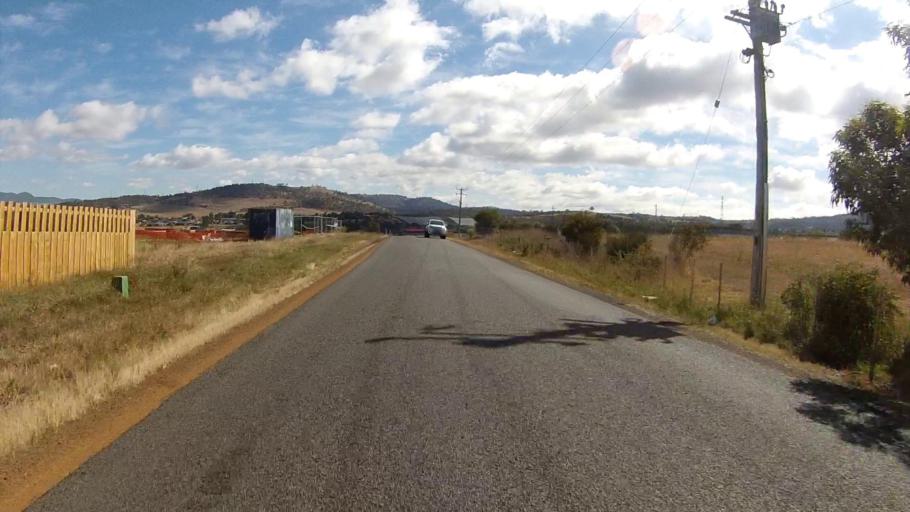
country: AU
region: Tasmania
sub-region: Brighton
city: Old Beach
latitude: -42.7624
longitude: 147.2786
